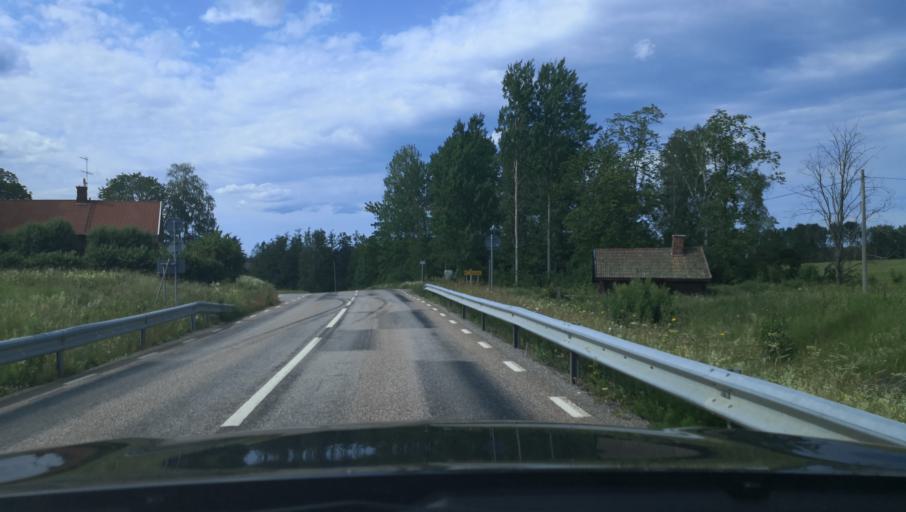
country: SE
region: Dalarna
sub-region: Avesta Kommun
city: Avesta
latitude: 59.9857
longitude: 16.1207
